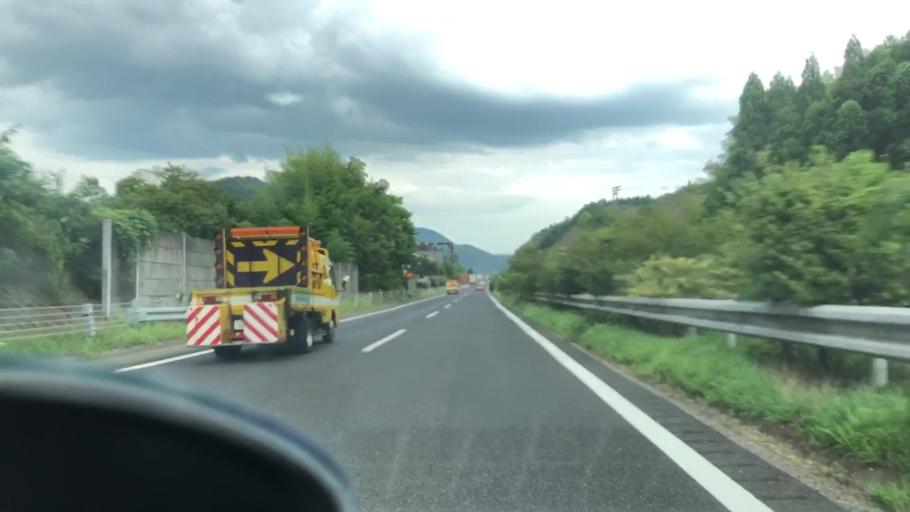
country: JP
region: Hyogo
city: Yamazakicho-nakabirose
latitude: 34.9739
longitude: 134.6530
